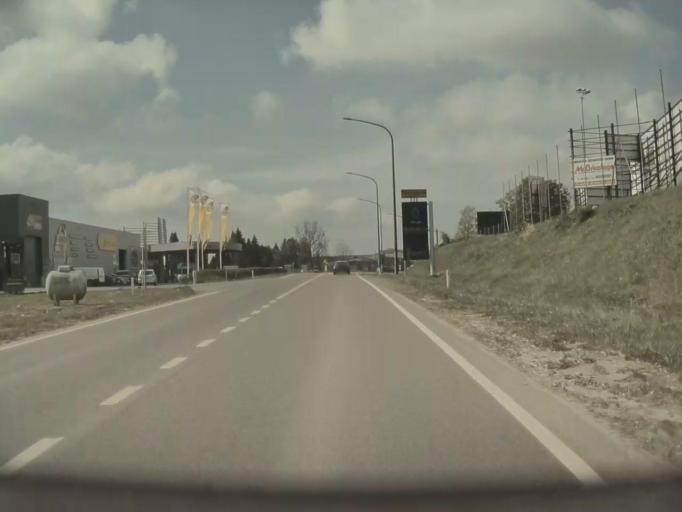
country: BE
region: Wallonia
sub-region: Province du Luxembourg
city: Marche-en-Famenne
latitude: 50.2091
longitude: 5.3137
